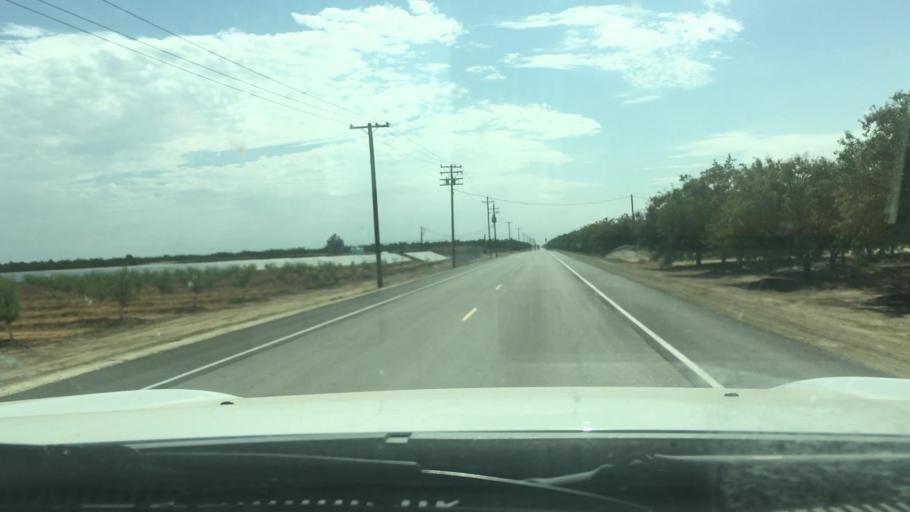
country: US
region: California
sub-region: Kern County
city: Wasco
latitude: 35.5576
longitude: -119.4704
